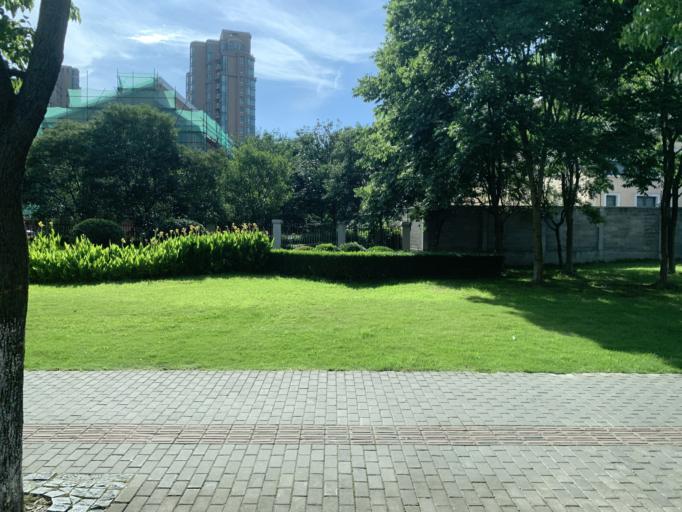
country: CN
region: Shanghai Shi
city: Huamu
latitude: 31.2090
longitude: 121.5322
